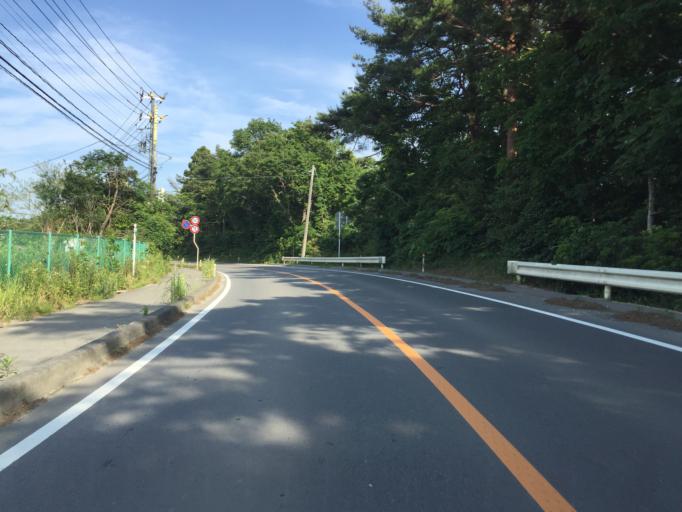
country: JP
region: Fukushima
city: Namie
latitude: 37.6690
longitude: 140.9960
